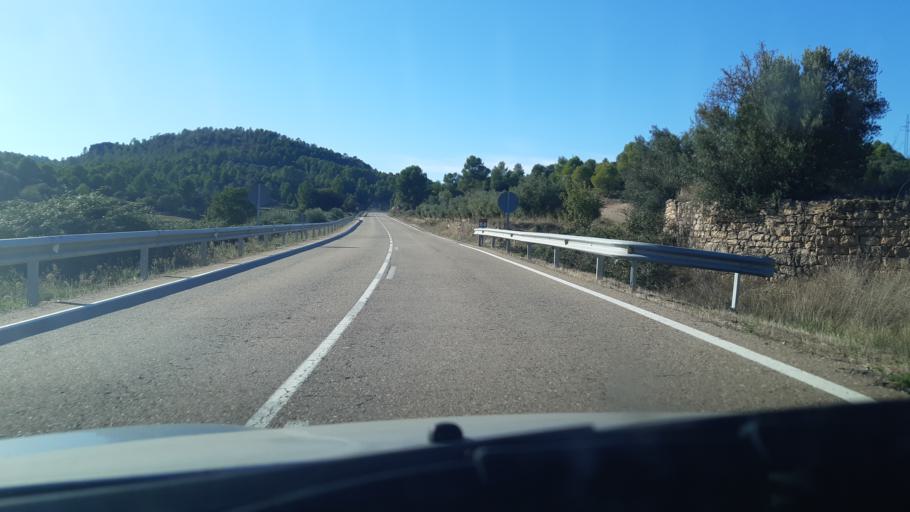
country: ES
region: Aragon
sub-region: Provincia de Teruel
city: Valjunquera
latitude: 40.9432
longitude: 0.0606
